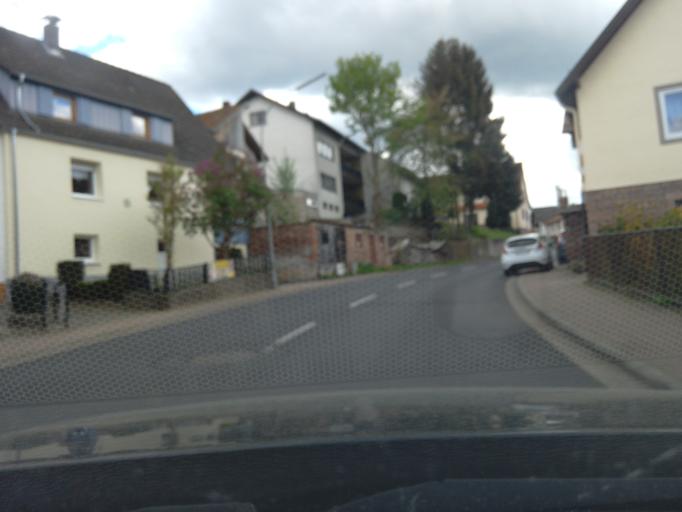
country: DE
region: Bavaria
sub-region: Regierungsbezirk Unterfranken
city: Aura im Sinngrund
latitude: 50.1898
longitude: 9.4727
